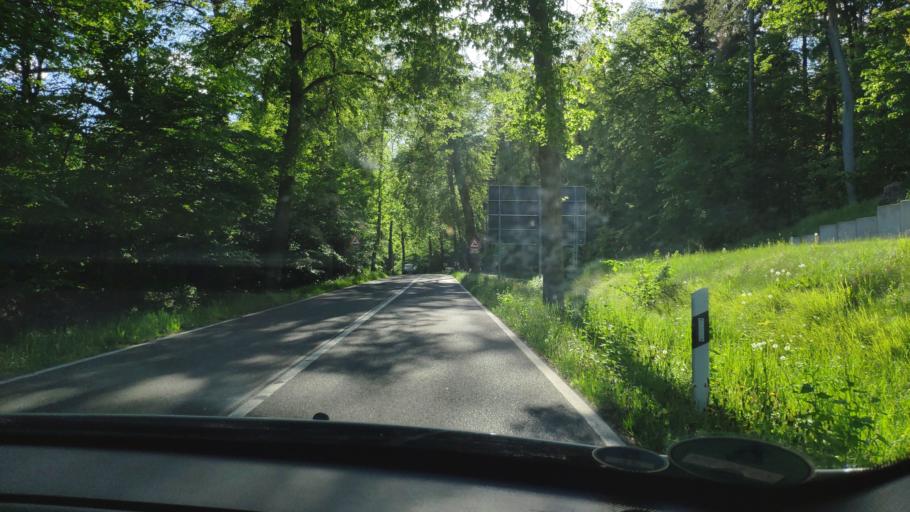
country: DE
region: Mecklenburg-Vorpommern
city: Neustrelitz
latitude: 53.3470
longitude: 13.0129
